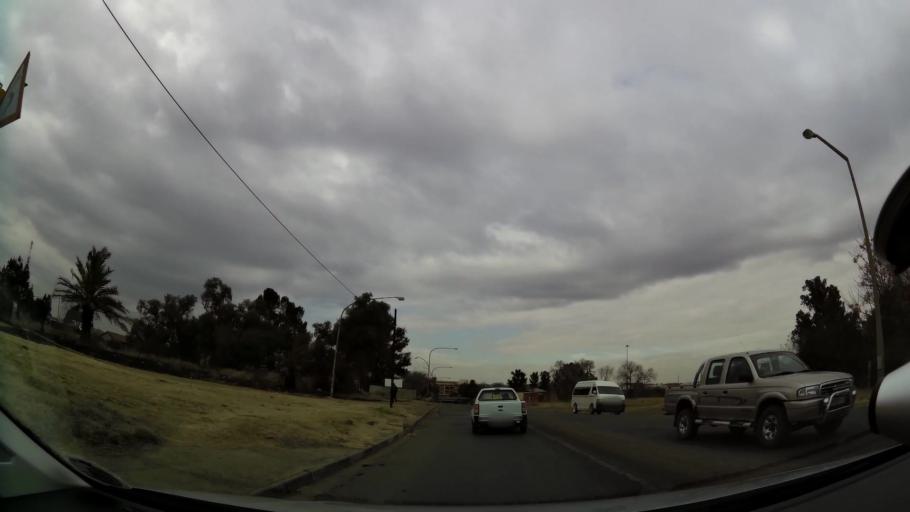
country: ZA
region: Orange Free State
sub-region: Fezile Dabi District Municipality
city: Kroonstad
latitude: -27.6585
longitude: 27.2306
